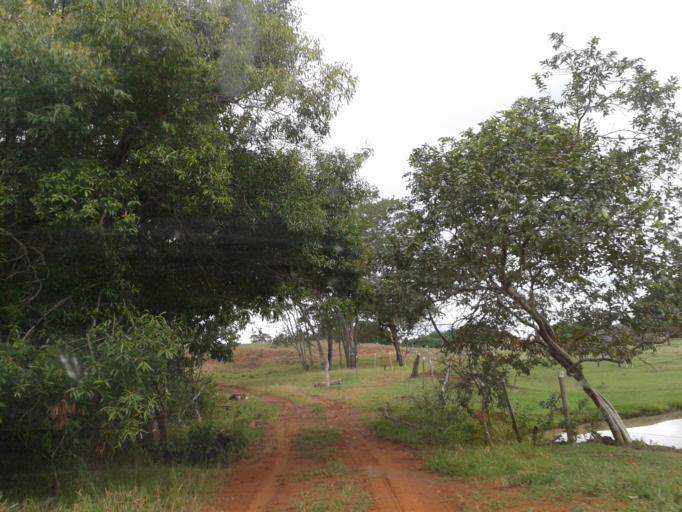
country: BR
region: Minas Gerais
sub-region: Campina Verde
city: Campina Verde
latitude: -19.4847
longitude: -49.6191
